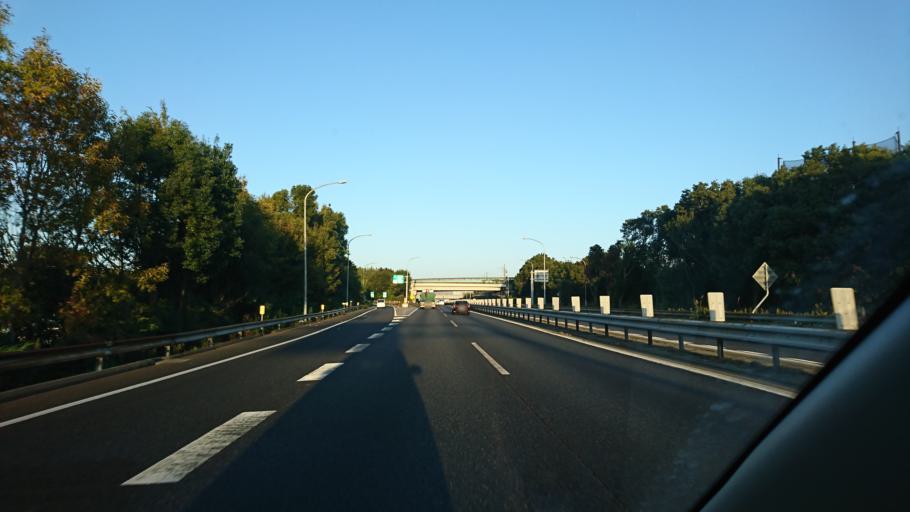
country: JP
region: Hyogo
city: Akashi
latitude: 34.7091
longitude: 134.9459
